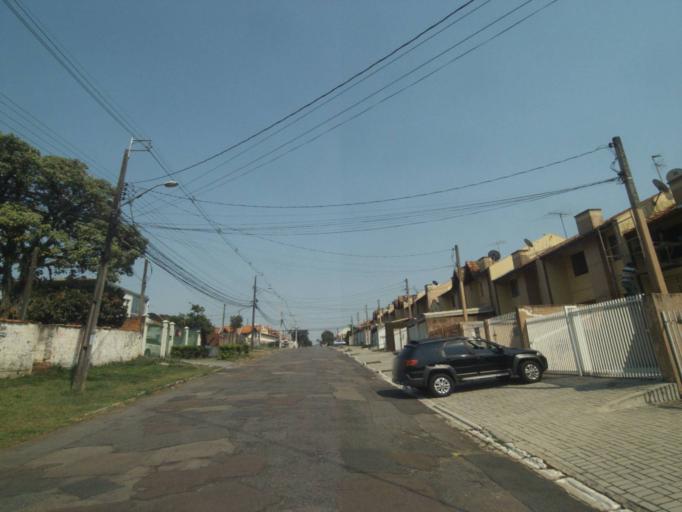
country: BR
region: Parana
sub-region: Sao Jose Dos Pinhais
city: Sao Jose dos Pinhais
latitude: -25.5195
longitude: -49.2522
